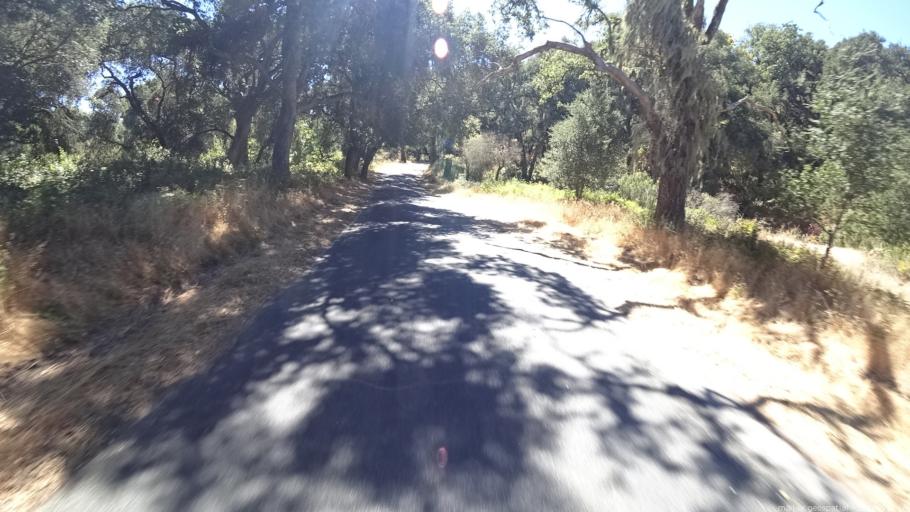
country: US
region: California
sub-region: Monterey County
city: Carmel Valley Village
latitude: 36.4424
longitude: -121.7971
